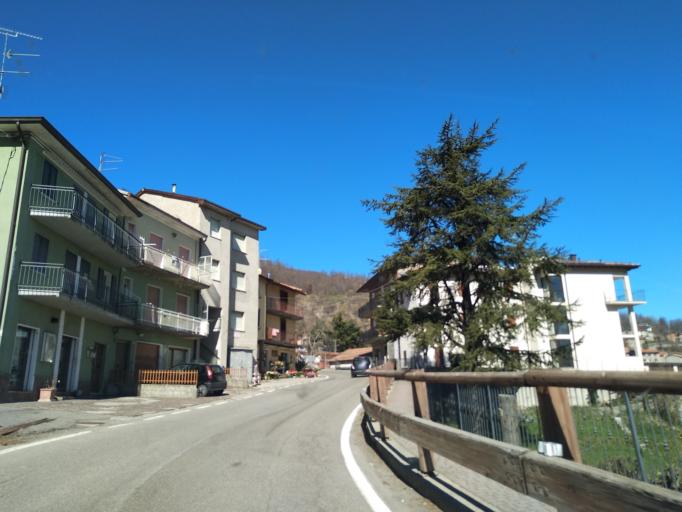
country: IT
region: Emilia-Romagna
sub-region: Provincia di Reggio Emilia
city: Ramiseto
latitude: 44.4124
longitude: 10.2722
